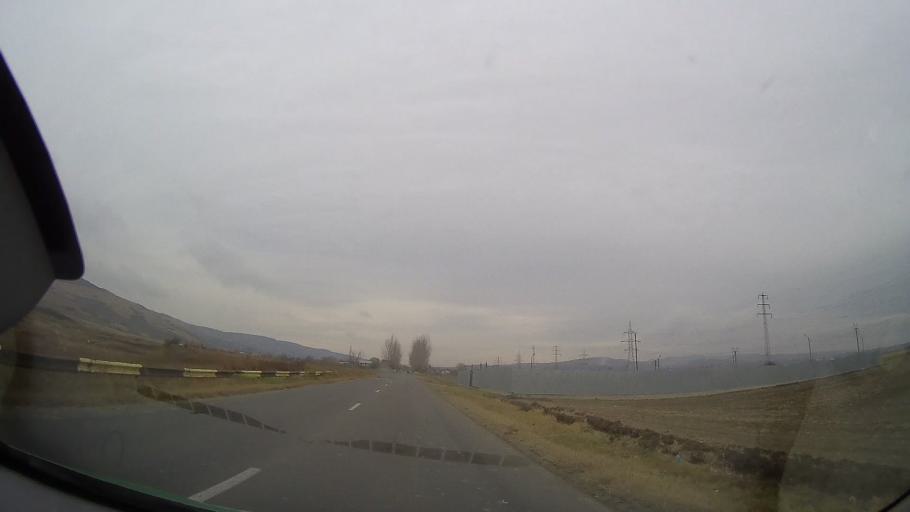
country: RO
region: Prahova
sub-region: Oras Urlati
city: Urlati
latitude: 44.9682
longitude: 26.2342
